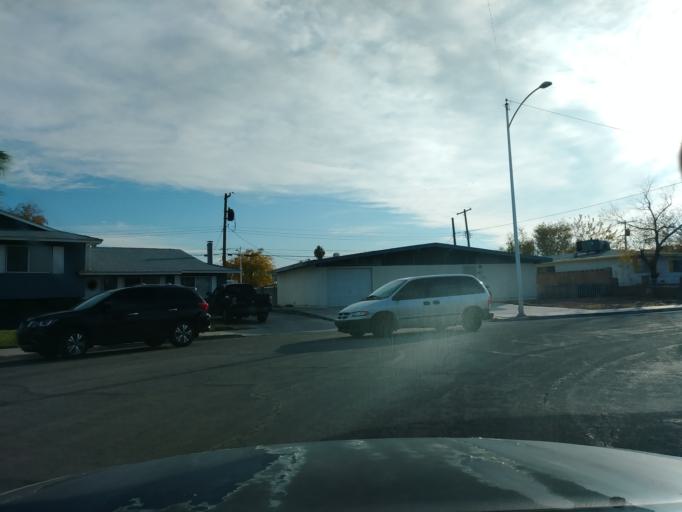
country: US
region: Nevada
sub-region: Clark County
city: Spring Valley
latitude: 36.1705
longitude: -115.2271
